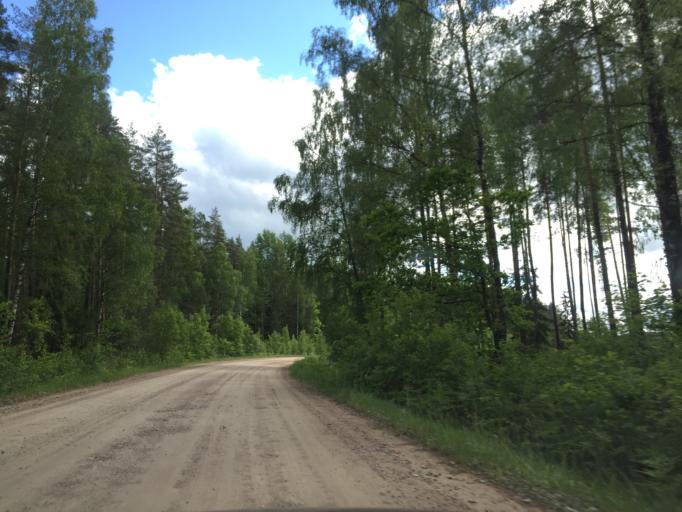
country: LV
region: Vecumnieki
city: Vecumnieki
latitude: 56.4929
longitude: 24.4090
